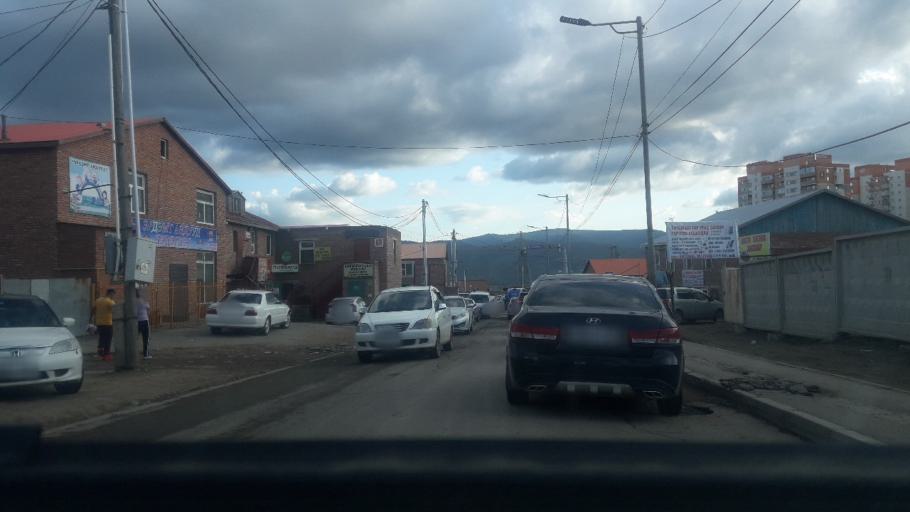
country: MN
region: Ulaanbaatar
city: Ulaanbaatar
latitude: 47.9233
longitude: 106.9960
